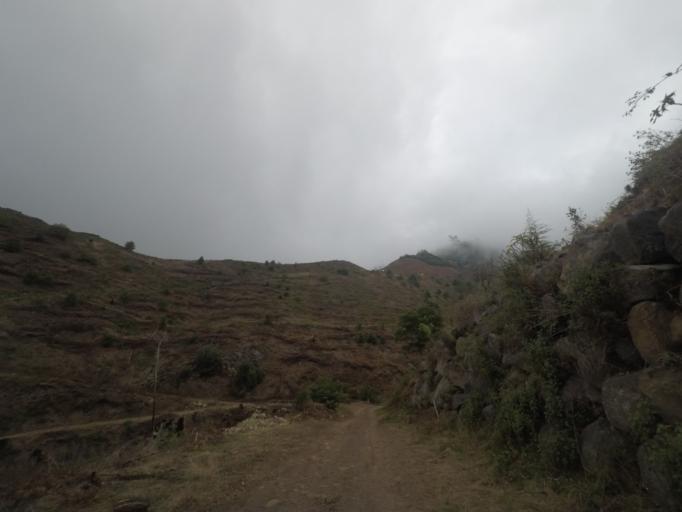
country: PT
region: Madeira
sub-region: Funchal
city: Nossa Senhora do Monte
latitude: 32.6956
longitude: -16.9103
